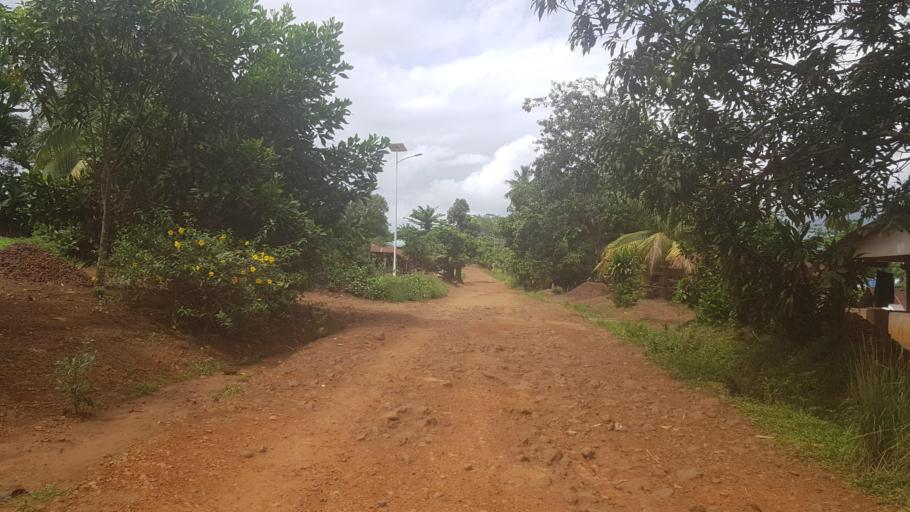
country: SL
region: Southern Province
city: Mogbwemo
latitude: 7.6029
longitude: -12.1761
